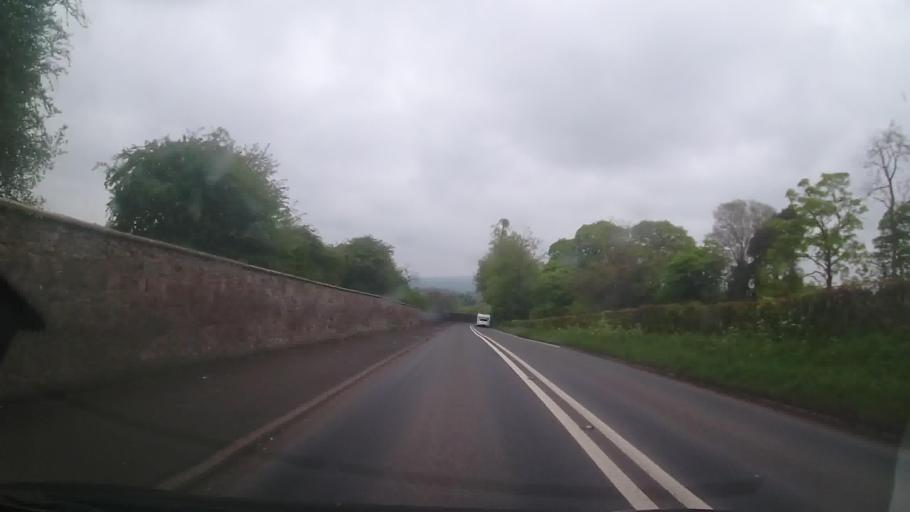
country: GB
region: Wales
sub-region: Wrexham
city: Ruabon
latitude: 52.9832
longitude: -3.0297
